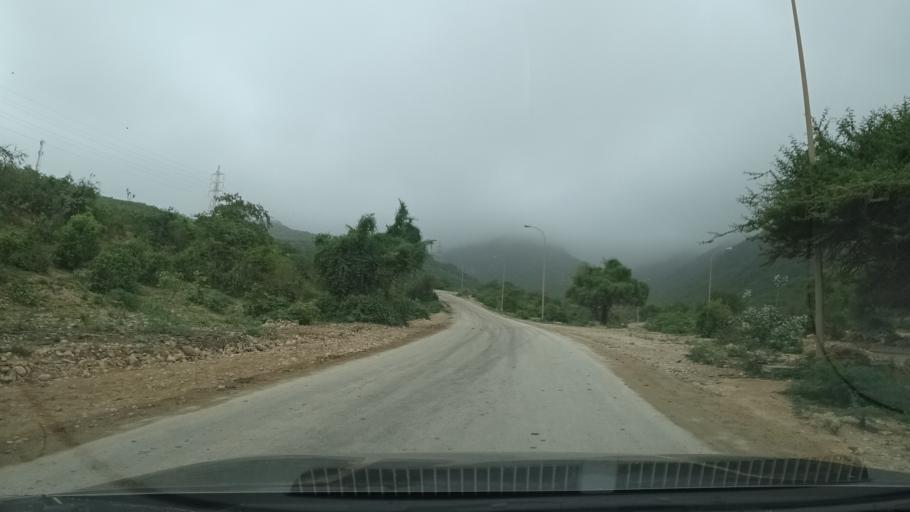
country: OM
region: Zufar
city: Salalah
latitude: 17.1007
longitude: 54.0769
